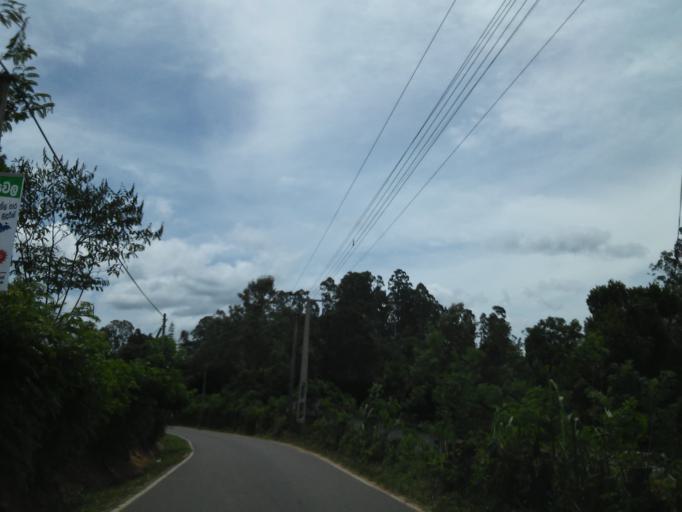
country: LK
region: Uva
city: Haputale
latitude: 6.8429
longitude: 81.0172
